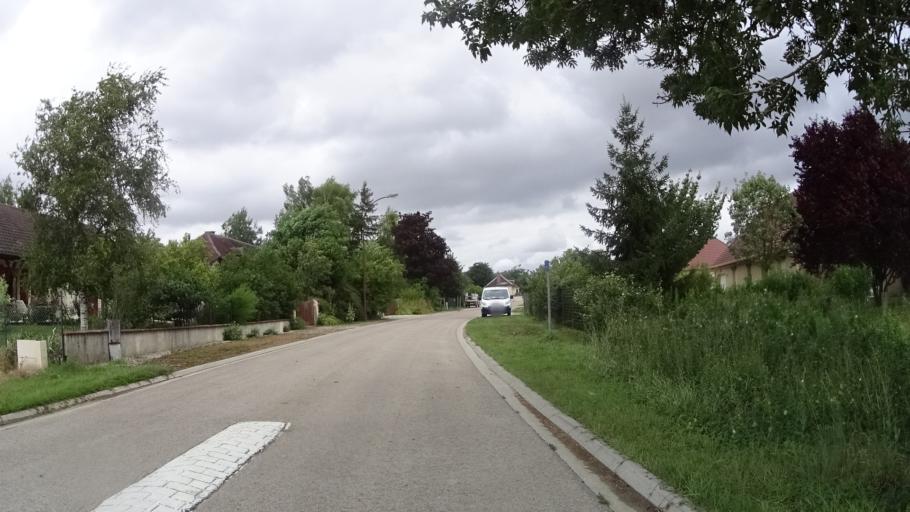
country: FR
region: Champagne-Ardenne
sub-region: Departement de l'Aube
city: Saint-Pouange
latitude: 48.1854
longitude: 4.0728
